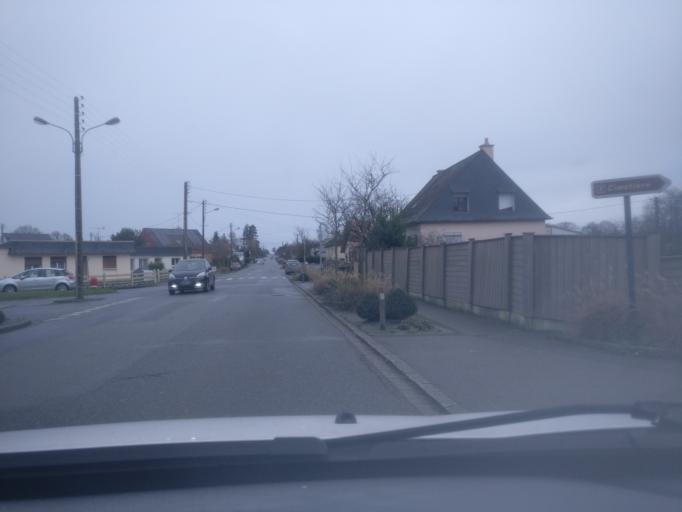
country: FR
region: Brittany
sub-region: Departement d'Ille-et-Vilaine
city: Louvigne-de-Bais
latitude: 48.0501
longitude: -1.3274
